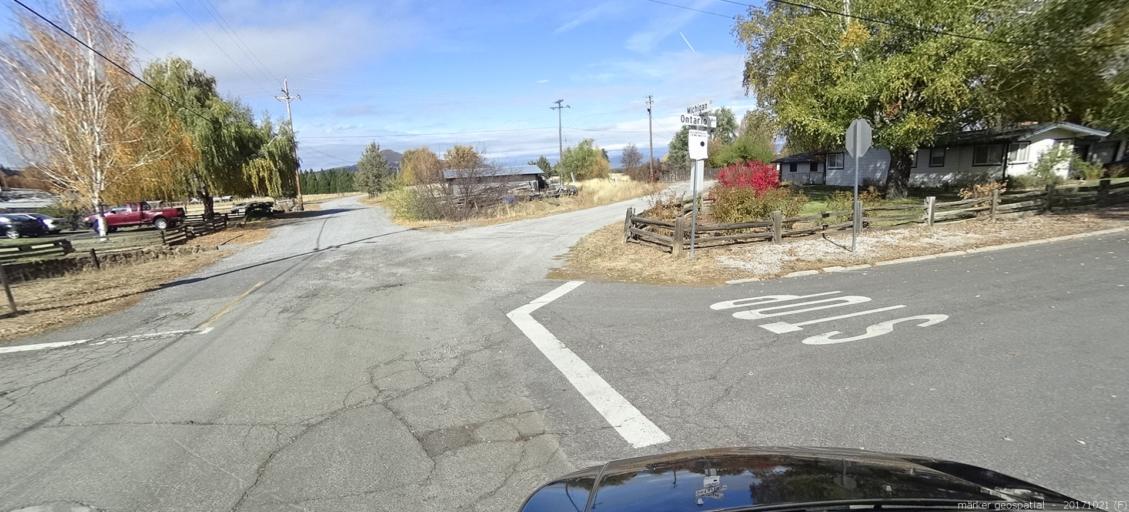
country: US
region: California
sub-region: Shasta County
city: Burney
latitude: 40.8840
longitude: -121.6643
